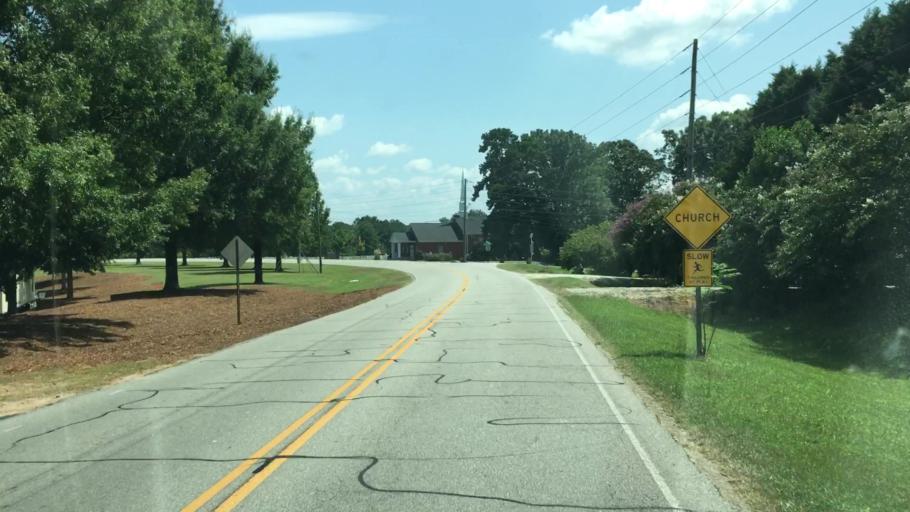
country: US
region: Georgia
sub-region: Oconee County
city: Watkinsville
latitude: 33.8610
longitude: -83.4583
